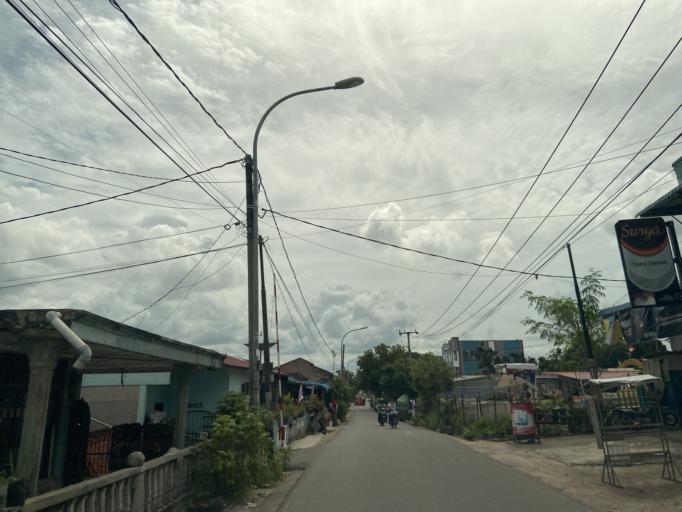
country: SG
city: Singapore
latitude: 1.0368
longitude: 103.9698
